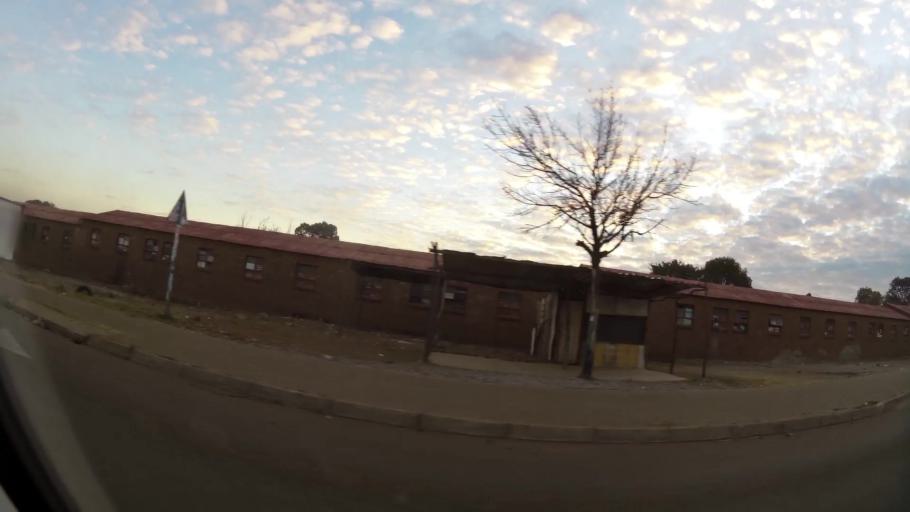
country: ZA
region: Gauteng
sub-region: City of Tshwane Metropolitan Municipality
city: Pretoria
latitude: -25.7103
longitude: 28.3325
